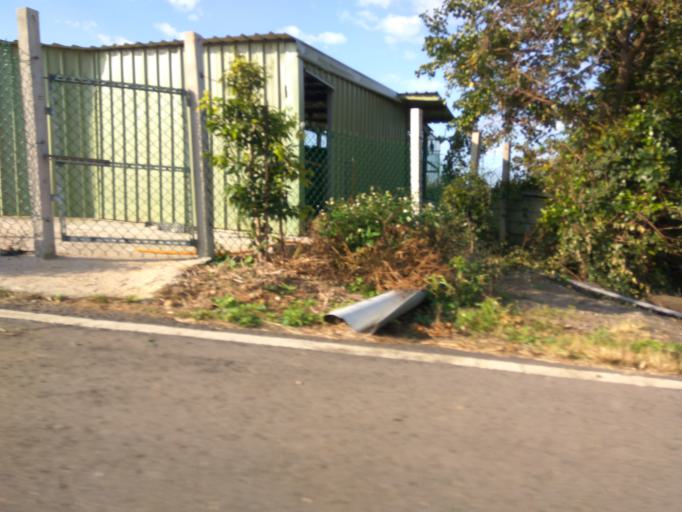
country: TW
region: Taiwan
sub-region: Hsinchu
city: Zhubei
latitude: 24.9767
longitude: 121.0600
